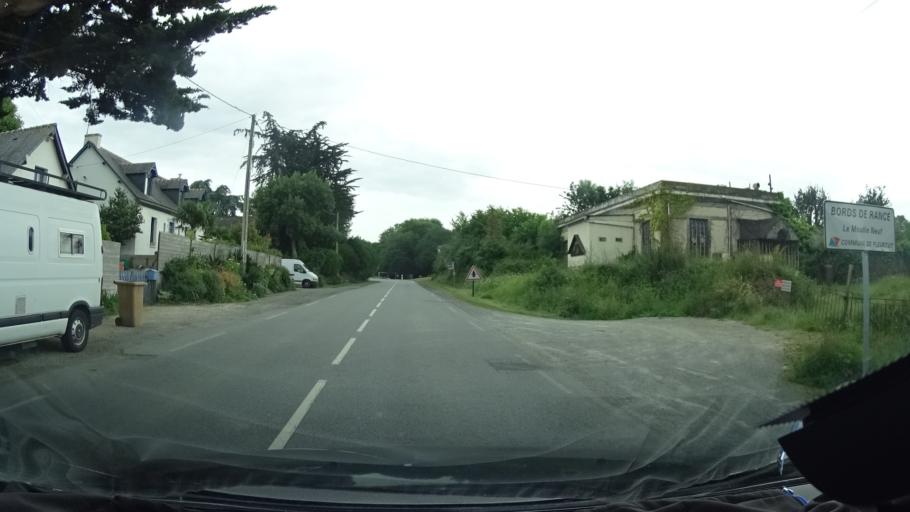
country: FR
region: Brittany
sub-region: Departement d'Ille-et-Vilaine
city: La Richardais
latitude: 48.6017
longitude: -2.0357
